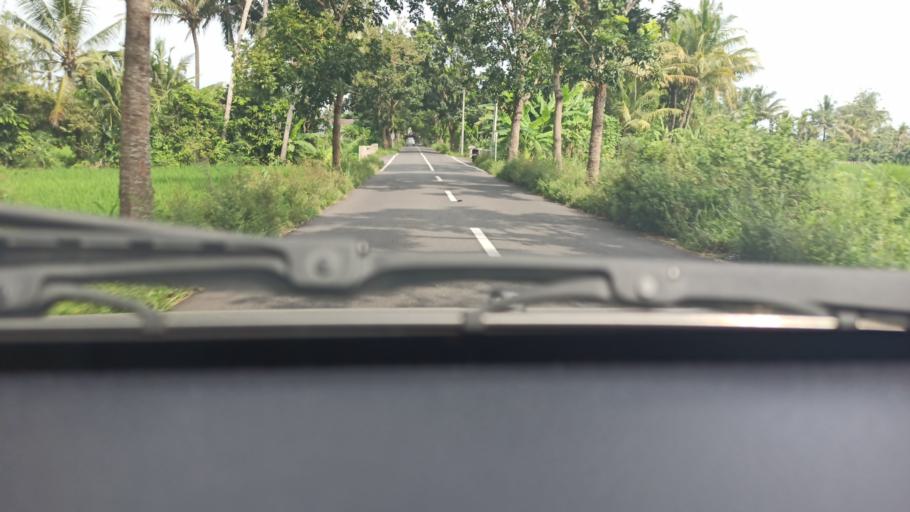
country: ID
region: Daerah Istimewa Yogyakarta
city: Sleman
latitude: -7.7020
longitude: 110.2984
